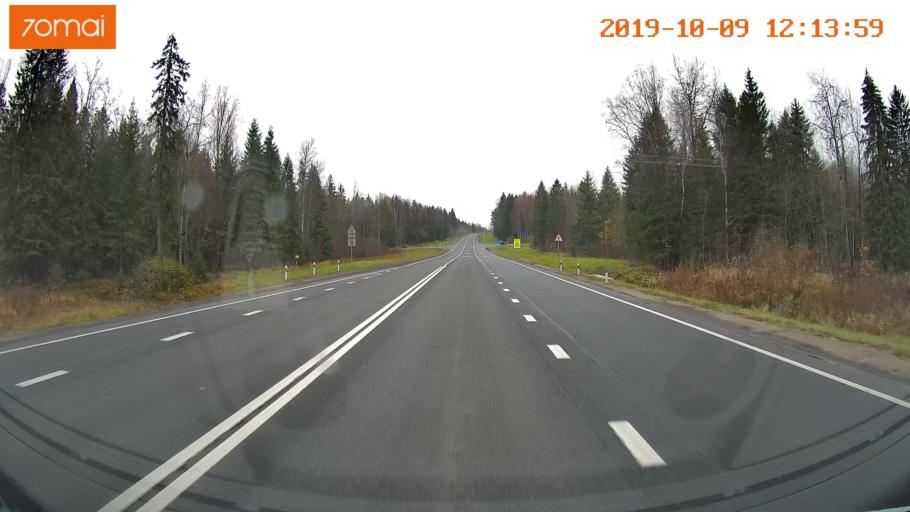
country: RU
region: Jaroslavl
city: Prechistoye
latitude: 58.5022
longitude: 40.3420
